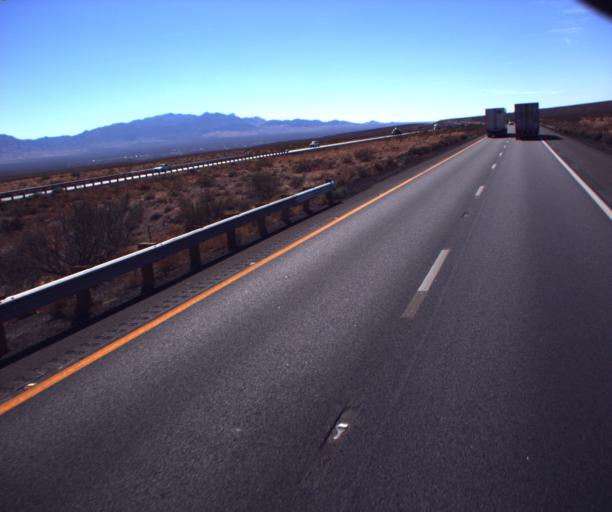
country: US
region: Arizona
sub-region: Mohave County
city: Beaver Dam
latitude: 36.8660
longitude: -113.9706
